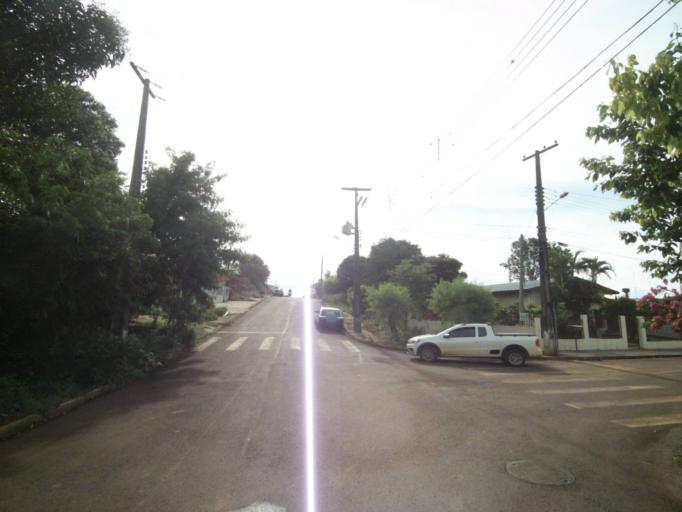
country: BR
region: Parana
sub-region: Guaraniacu
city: Guaraniacu
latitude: -25.1041
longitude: -52.8648
